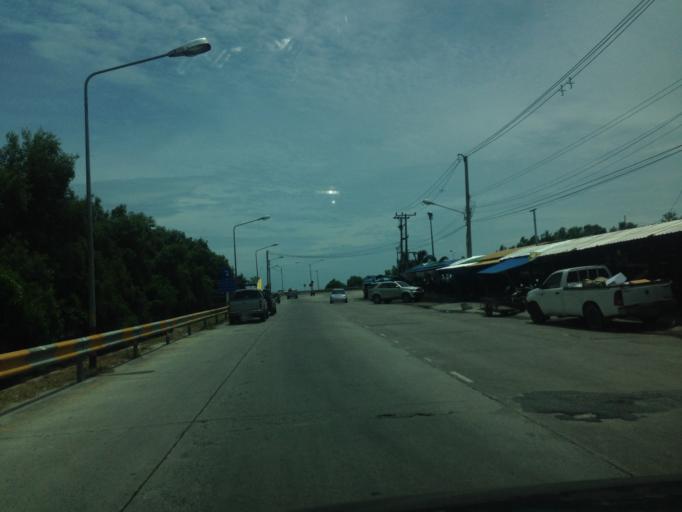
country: TH
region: Chon Buri
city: Chon Buri
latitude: 13.3742
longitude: 100.9792
